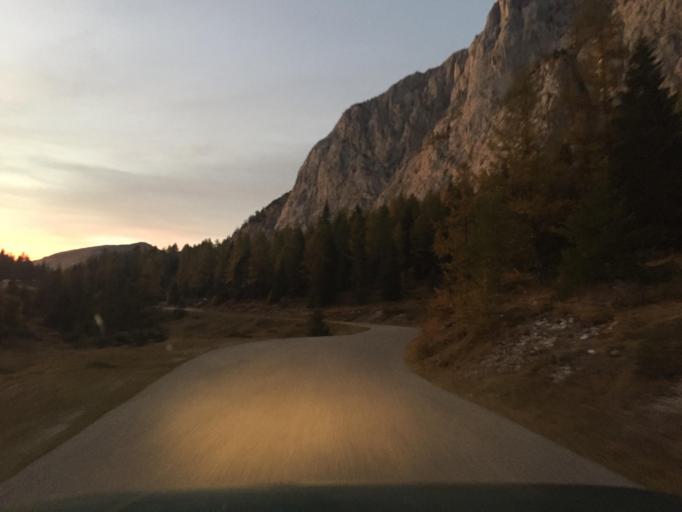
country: IT
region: Veneto
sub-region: Provincia di Belluno
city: Granvilla
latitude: 46.6219
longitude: 12.7126
